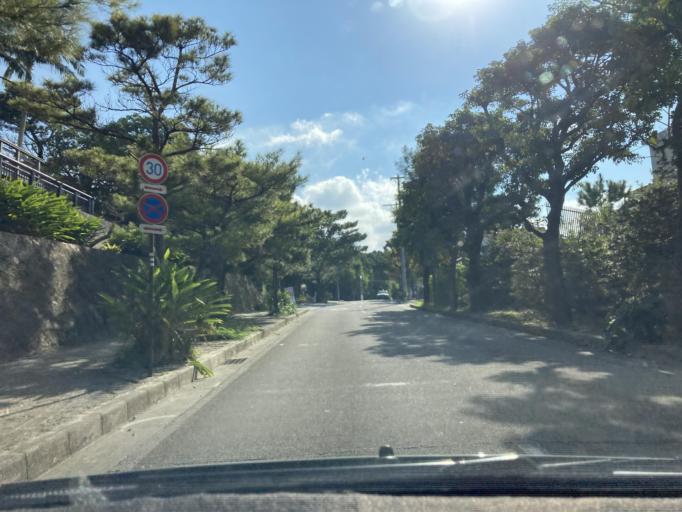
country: JP
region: Okinawa
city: Naha-shi
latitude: 26.2176
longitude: 127.7161
